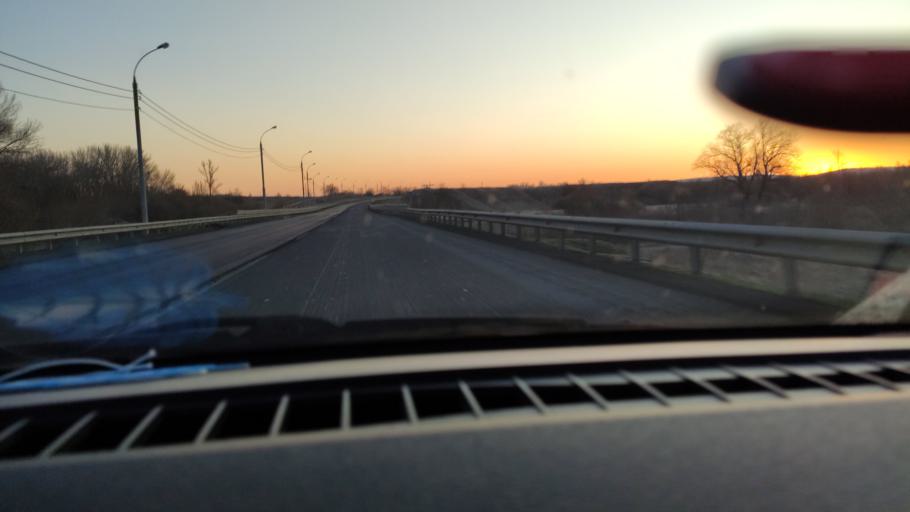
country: RU
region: Saratov
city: Yelshanka
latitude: 51.8246
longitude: 46.2198
